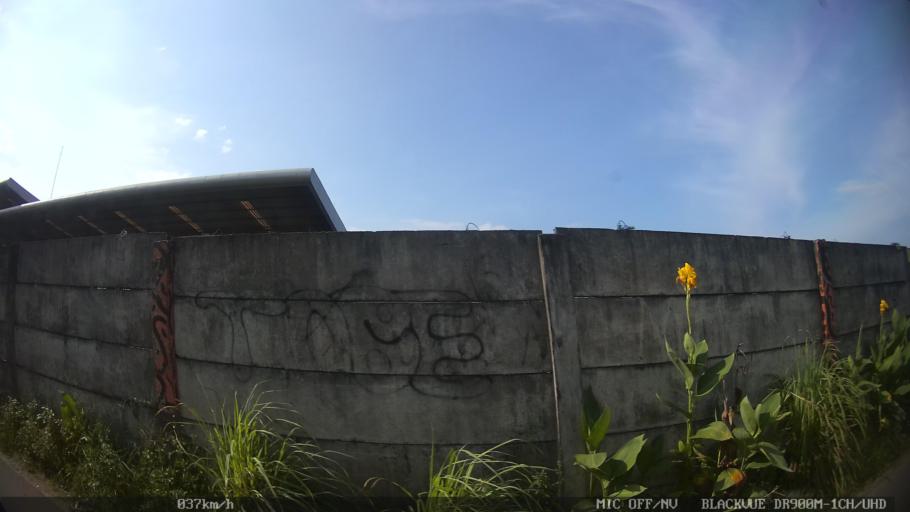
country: ID
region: North Sumatra
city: Medan
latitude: 3.5939
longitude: 98.7580
